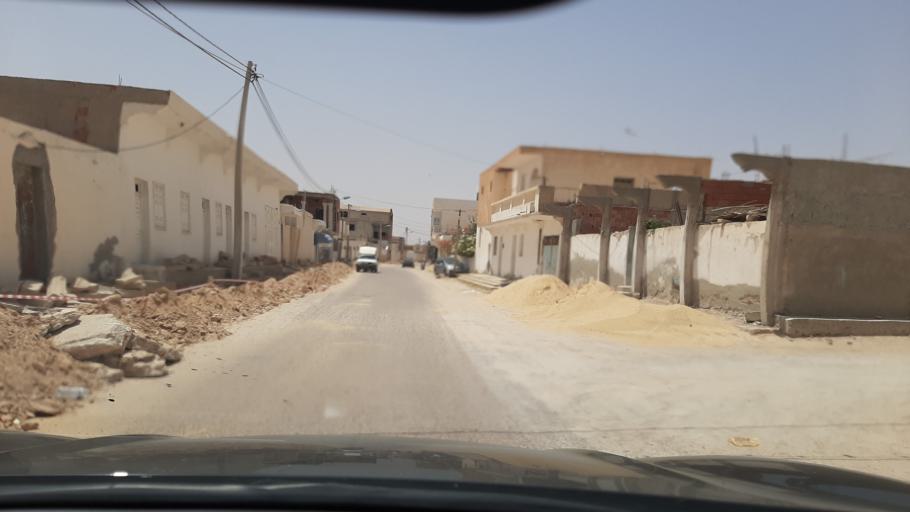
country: TN
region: Qabis
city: Matmata
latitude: 33.6175
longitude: 10.2777
